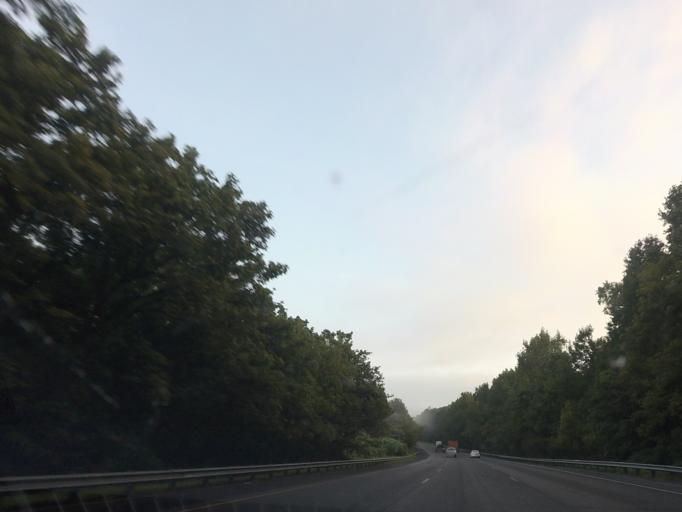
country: US
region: Georgia
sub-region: Monroe County
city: Forsyth
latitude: 33.0861
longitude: -83.9920
